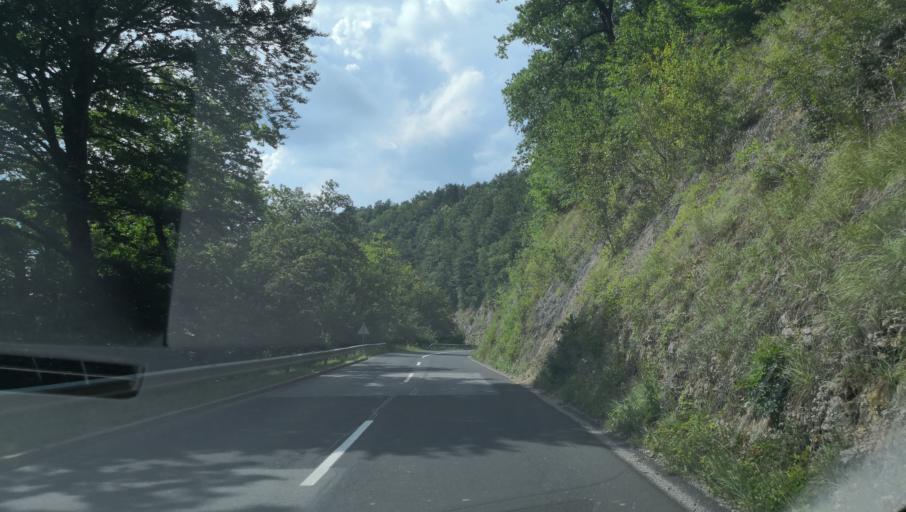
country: SI
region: Zuzemberk
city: Zuzemberk
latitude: 45.8518
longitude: 14.8986
